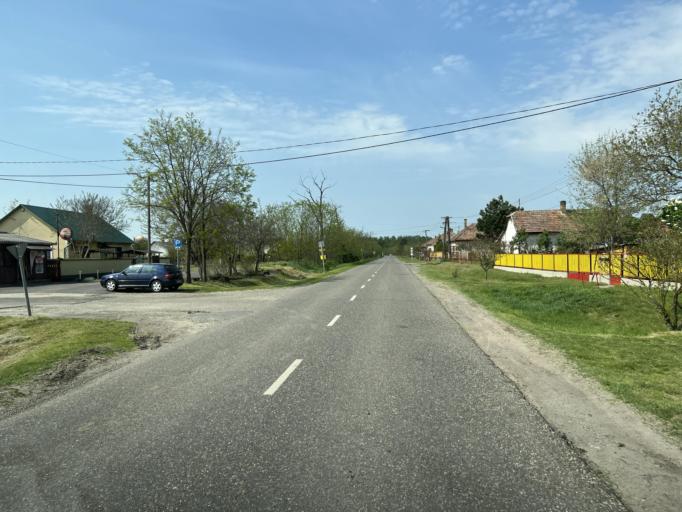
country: HU
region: Pest
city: Tortel
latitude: 47.1142
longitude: 19.9210
